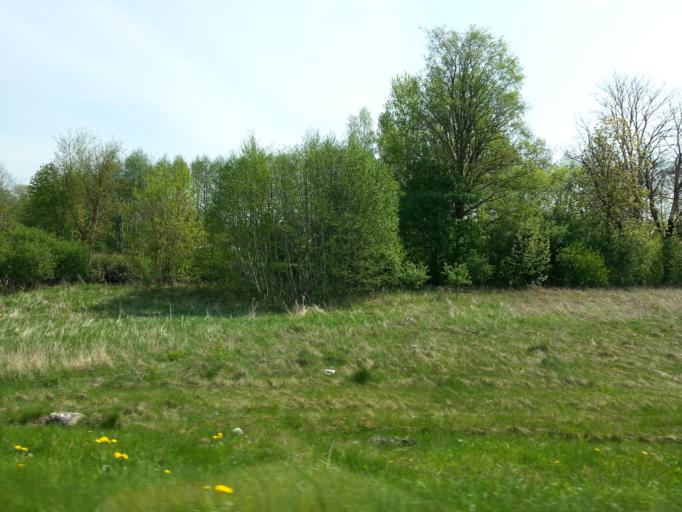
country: LT
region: Panevezys
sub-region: Panevezys City
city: Panevezys
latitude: 55.8097
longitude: 24.2704
